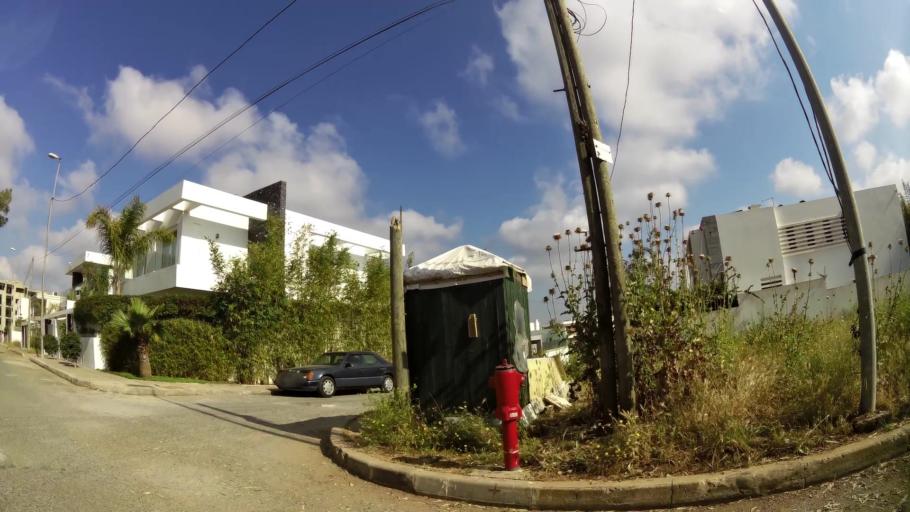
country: MA
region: Rabat-Sale-Zemmour-Zaer
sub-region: Skhirate-Temara
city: Temara
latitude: 33.9538
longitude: -6.8781
